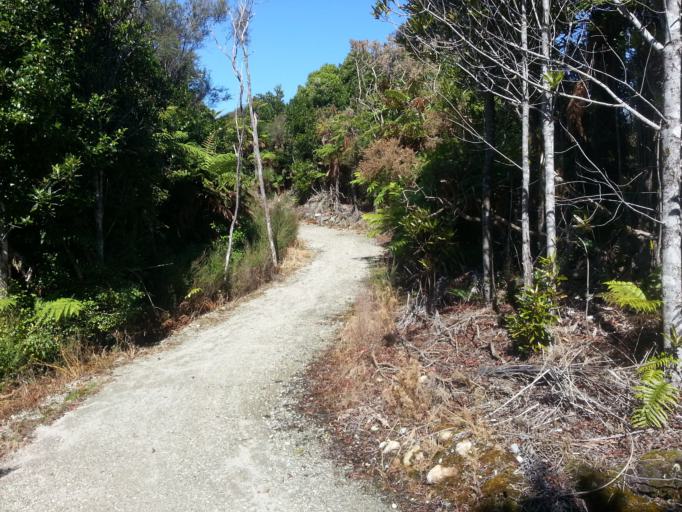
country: NZ
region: West Coast
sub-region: Grey District
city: Greymouth
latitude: -42.6577
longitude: 171.1964
